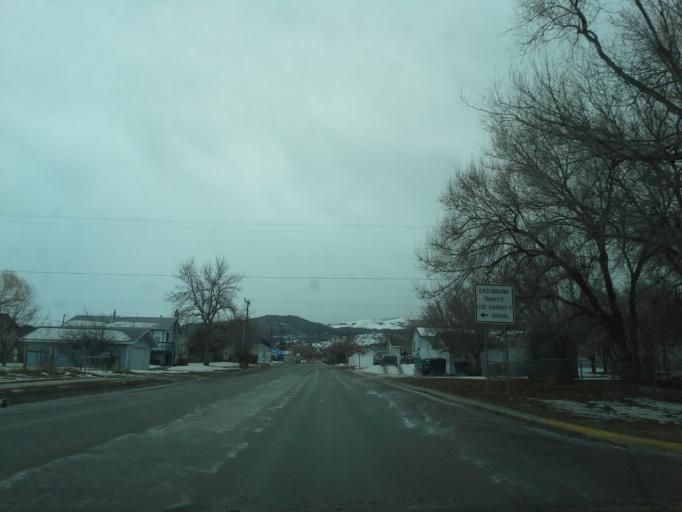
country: US
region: Montana
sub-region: Lewis and Clark County
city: Helena
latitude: 46.6098
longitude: -112.0151
